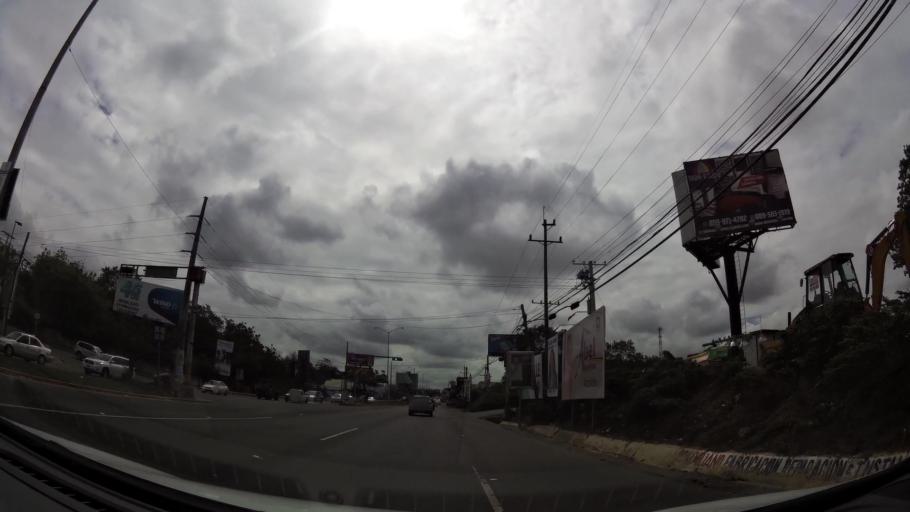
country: DO
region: Santiago
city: Santiago de los Caballeros
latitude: 19.4427
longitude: -70.6697
